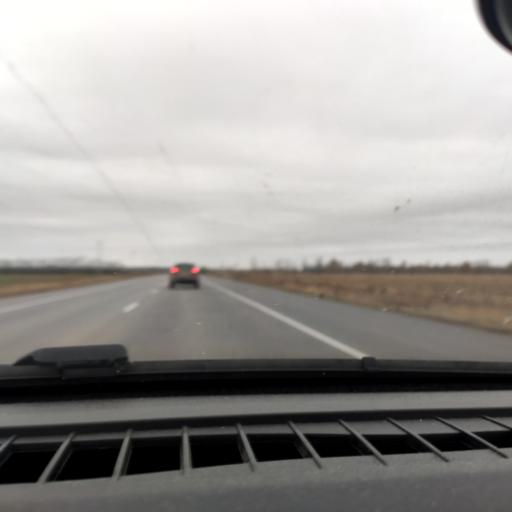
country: RU
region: Voronezj
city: Devitsa
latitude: 51.5651
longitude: 38.9739
